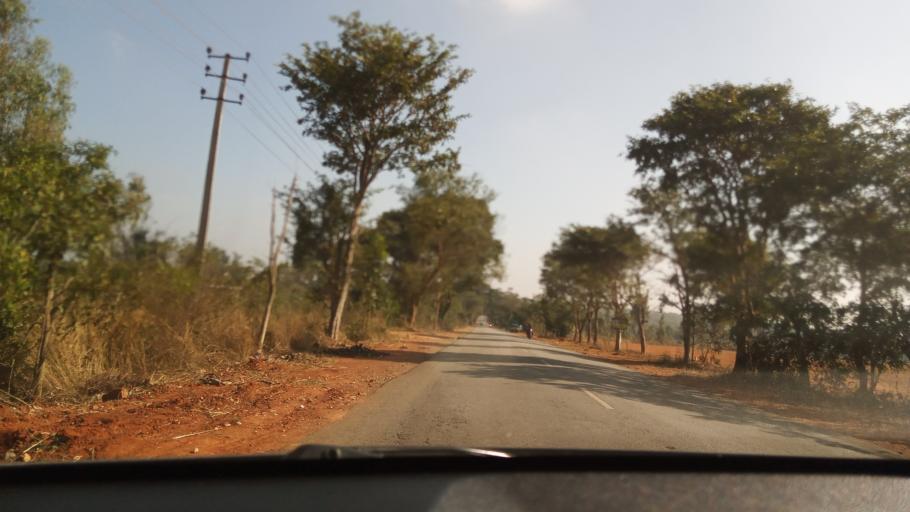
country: IN
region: Karnataka
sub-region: Bangalore Rural
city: Devanhalli
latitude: 13.2626
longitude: 77.7347
